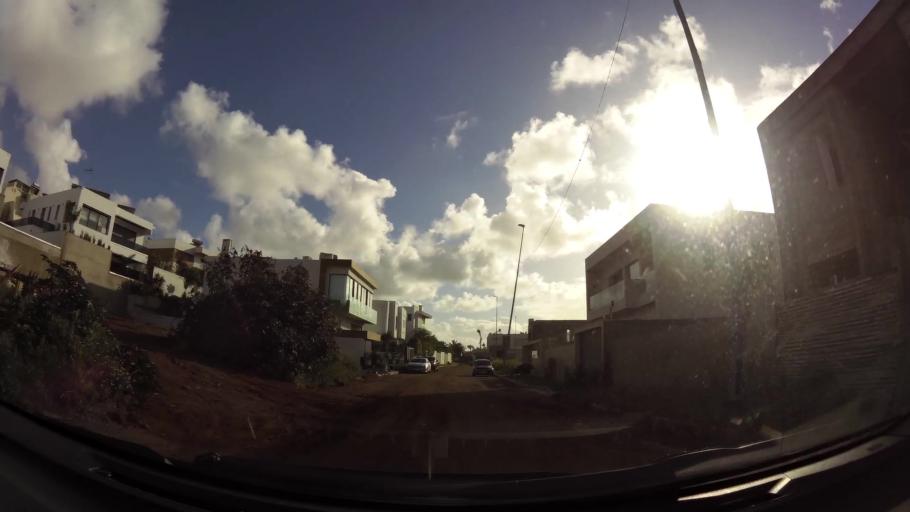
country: MA
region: Grand Casablanca
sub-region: Casablanca
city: Casablanca
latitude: 33.5754
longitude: -7.6889
